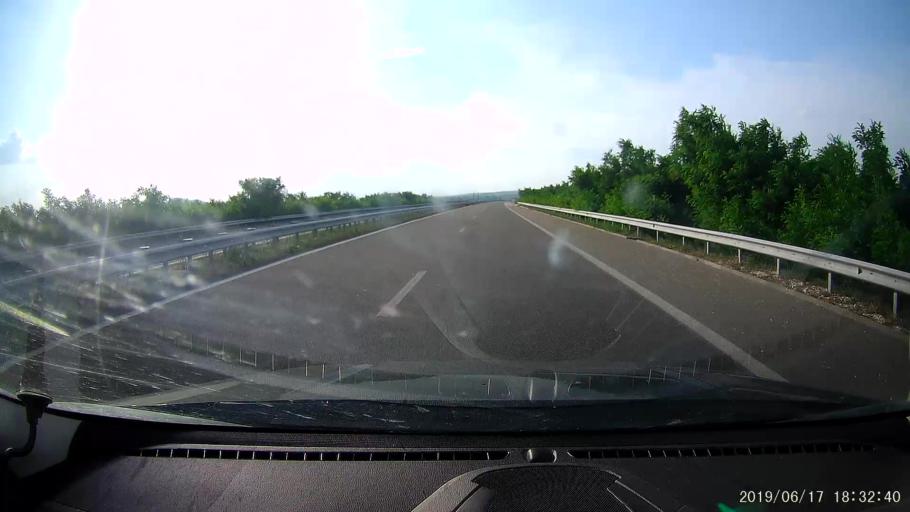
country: BG
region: Khaskovo
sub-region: Obshtina Dimitrovgrad
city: Dimitrovgrad
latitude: 42.0637
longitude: 25.4736
